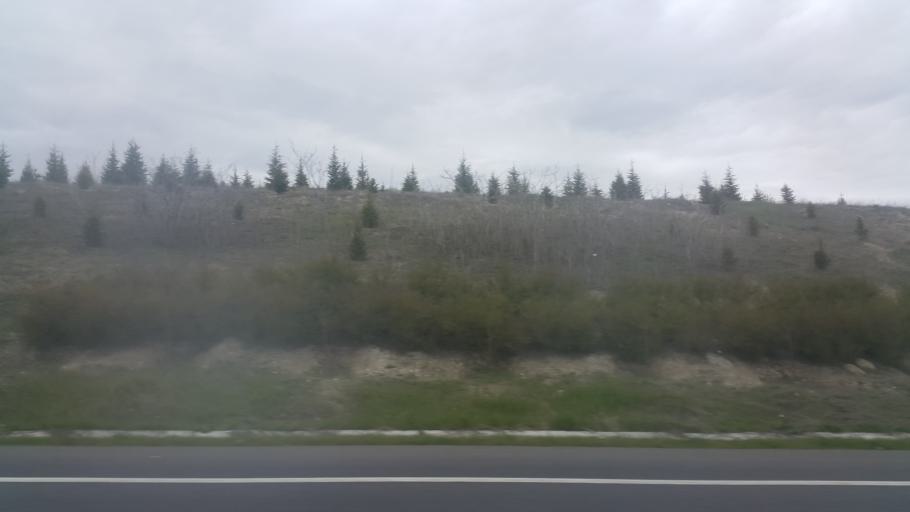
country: TR
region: Ankara
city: Etimesgut
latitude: 39.8986
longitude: 32.6219
